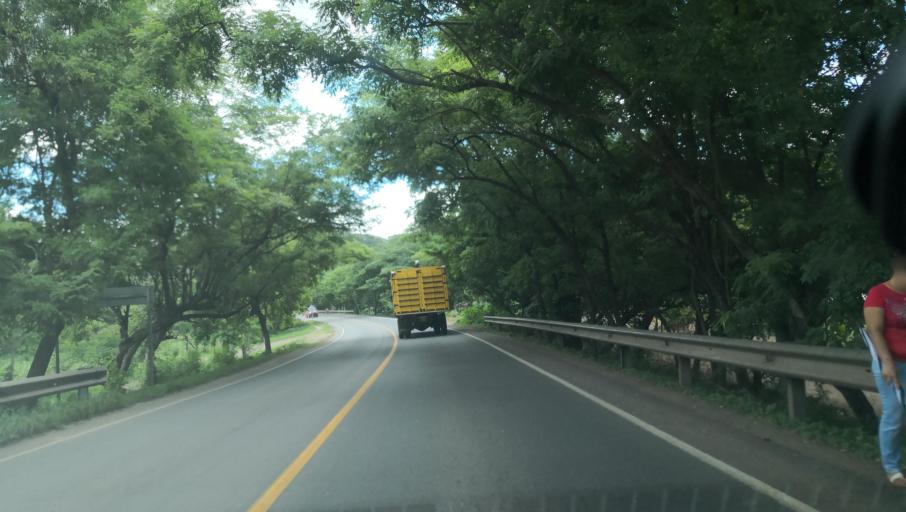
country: NI
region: Madriz
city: Yalaguina
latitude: 13.4720
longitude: -86.4762
